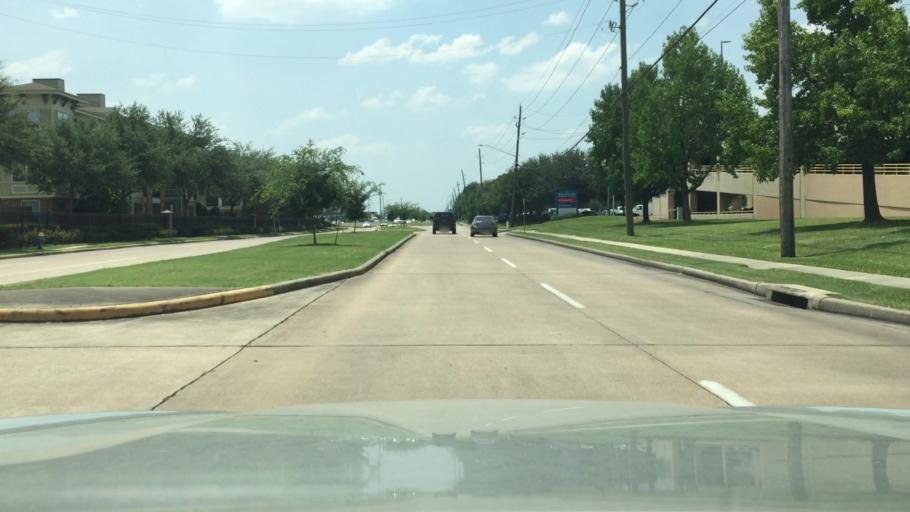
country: US
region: Texas
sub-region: Harris County
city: Bunker Hill Village
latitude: 29.7290
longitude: -95.5925
